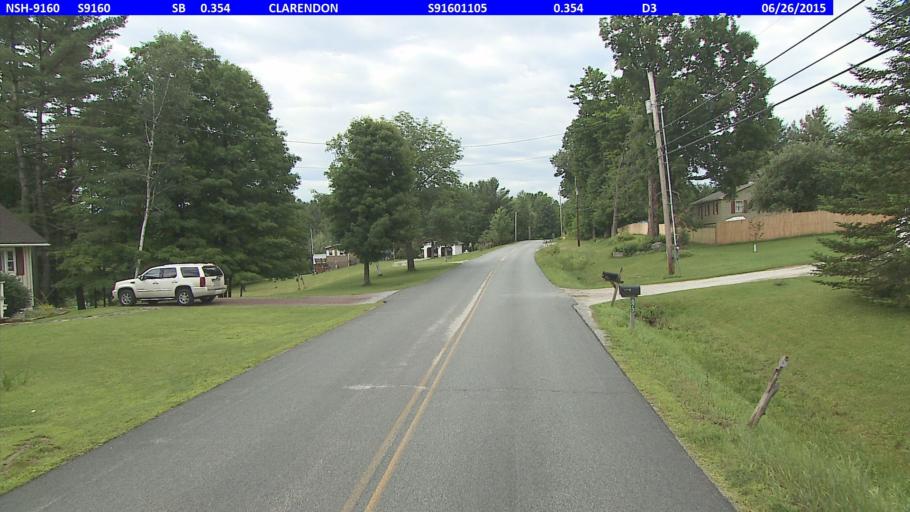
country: US
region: Vermont
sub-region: Rutland County
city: Rutland
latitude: 43.5327
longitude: -72.9456
